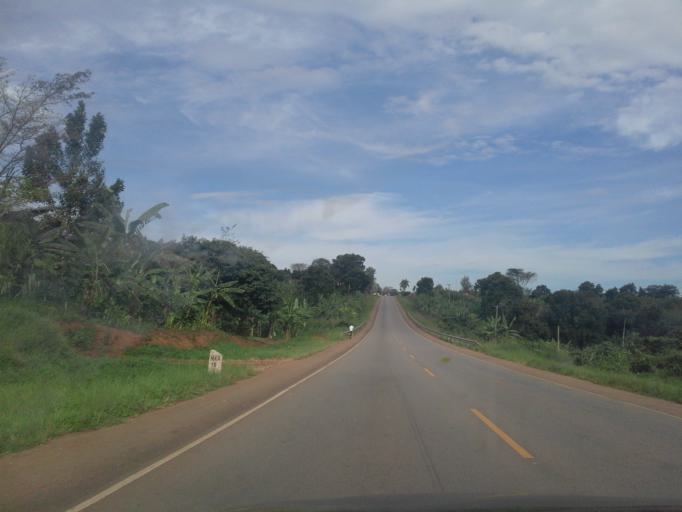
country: UG
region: Central Region
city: Masaka
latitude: -0.3467
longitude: 31.6146
